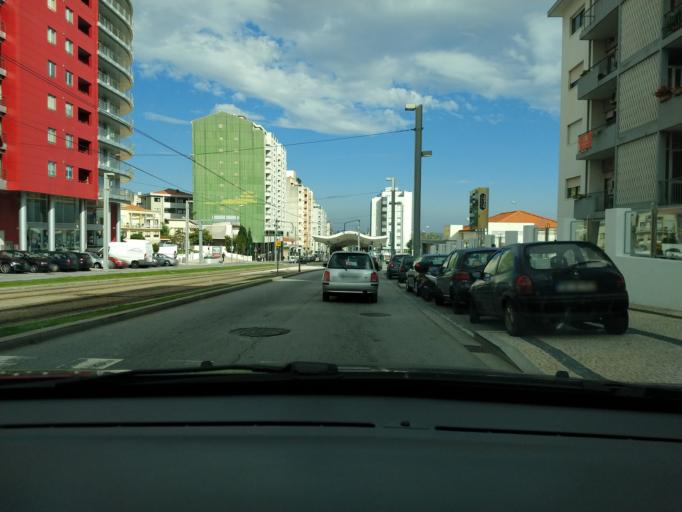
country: PT
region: Porto
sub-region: Vila Nova de Gaia
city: Vilar de Andorinho
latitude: 41.1183
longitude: -8.6063
